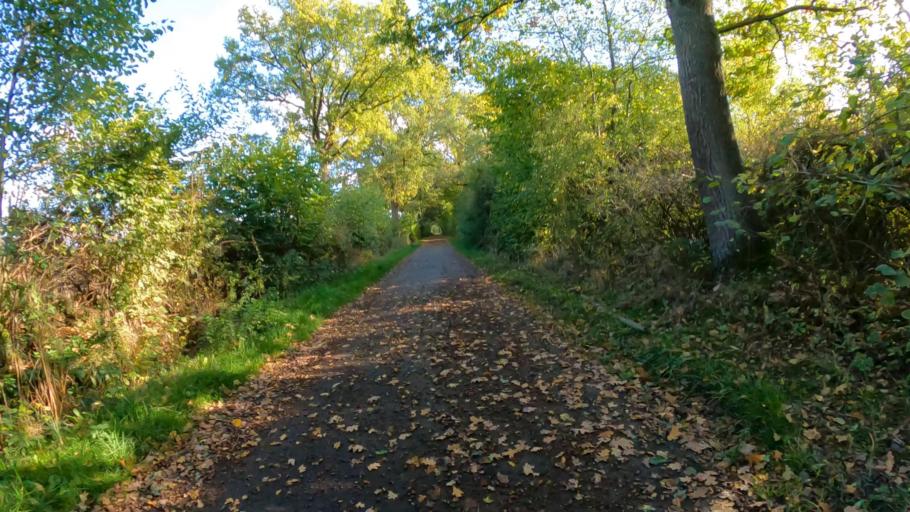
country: DE
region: Schleswig-Holstein
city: Delingsdorf
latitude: 53.6905
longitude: 10.2691
